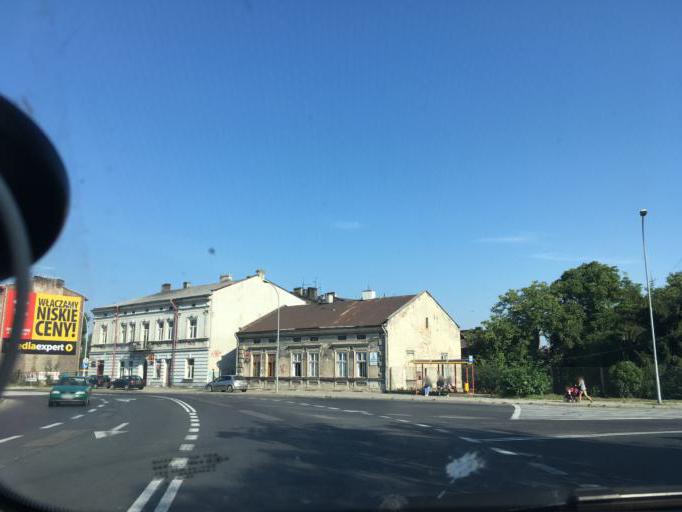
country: PL
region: Subcarpathian Voivodeship
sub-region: Przemysl
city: Przemysl
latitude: 49.7825
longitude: 22.7909
